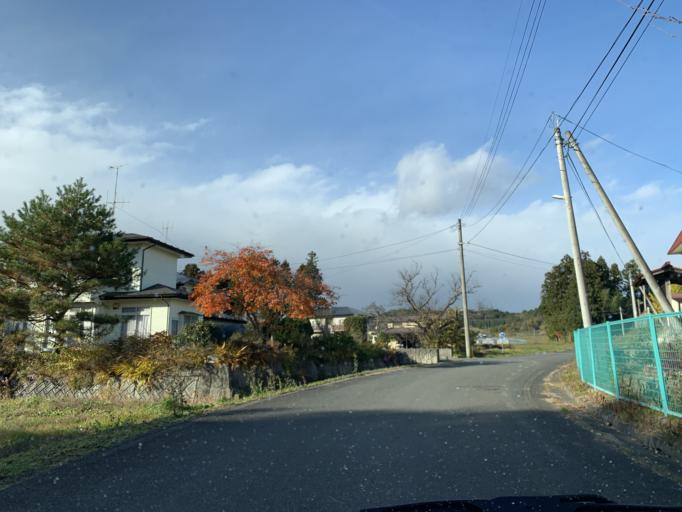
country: JP
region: Iwate
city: Ichinoseki
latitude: 39.0096
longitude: 141.1038
